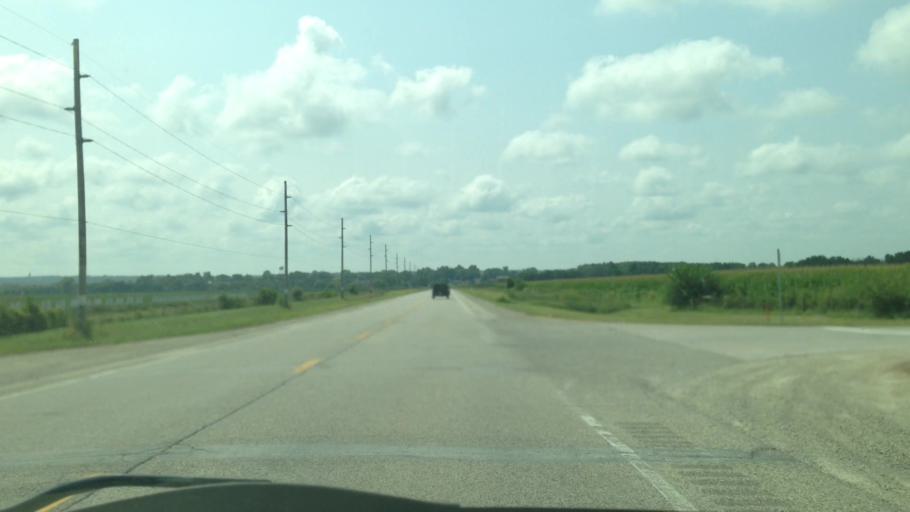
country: US
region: Iowa
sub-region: Benton County
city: Walford
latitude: 41.8143
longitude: -91.8722
